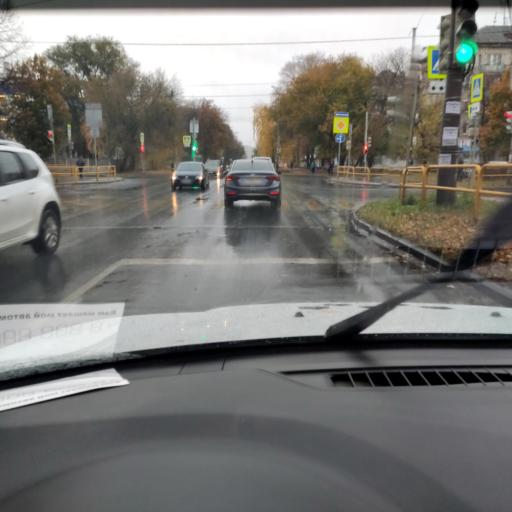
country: RU
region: Samara
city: Tol'yatti
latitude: 53.5055
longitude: 49.4122
